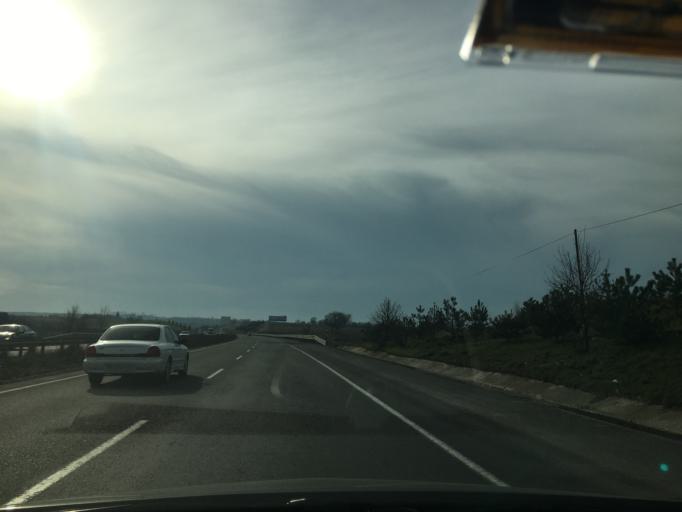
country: TR
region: Istanbul
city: Buyukcavuslu
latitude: 41.2415
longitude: 28.0426
